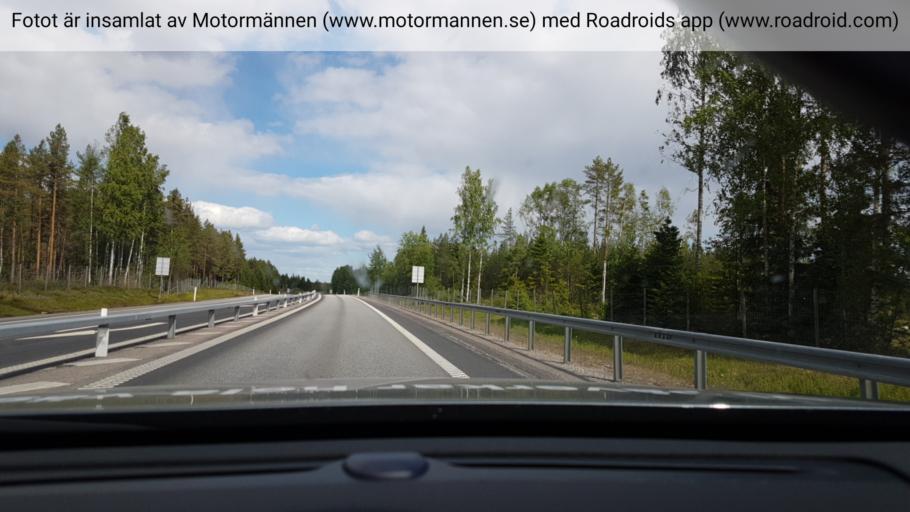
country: SE
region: Vaesterbotten
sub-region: Umea Kommun
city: Hoernefors
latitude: 63.6183
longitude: 19.8349
